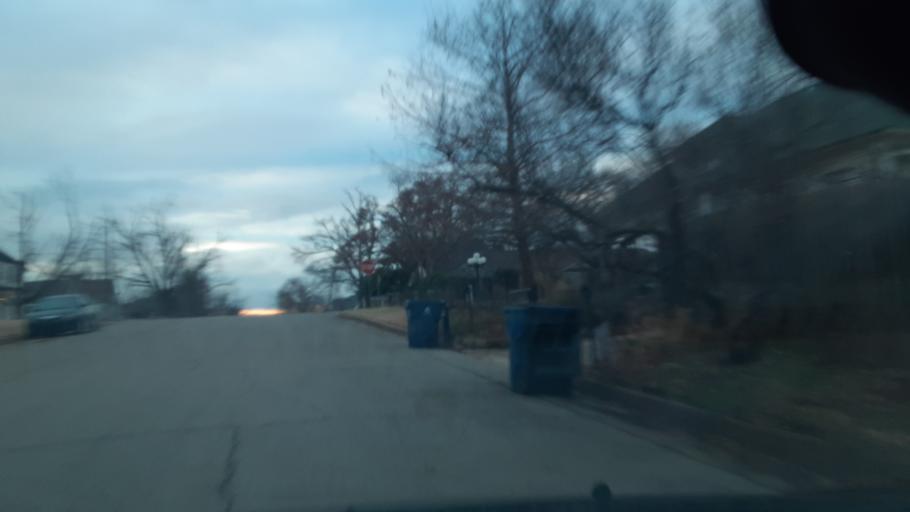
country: US
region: Oklahoma
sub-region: Logan County
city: Guthrie
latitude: 35.8833
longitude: -97.4184
